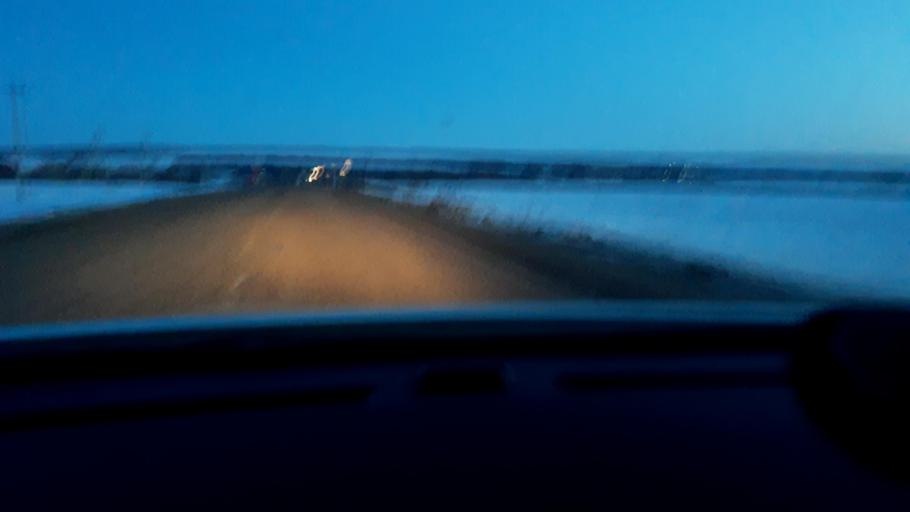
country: RU
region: Bashkortostan
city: Avdon
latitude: 54.3947
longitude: 55.7068
